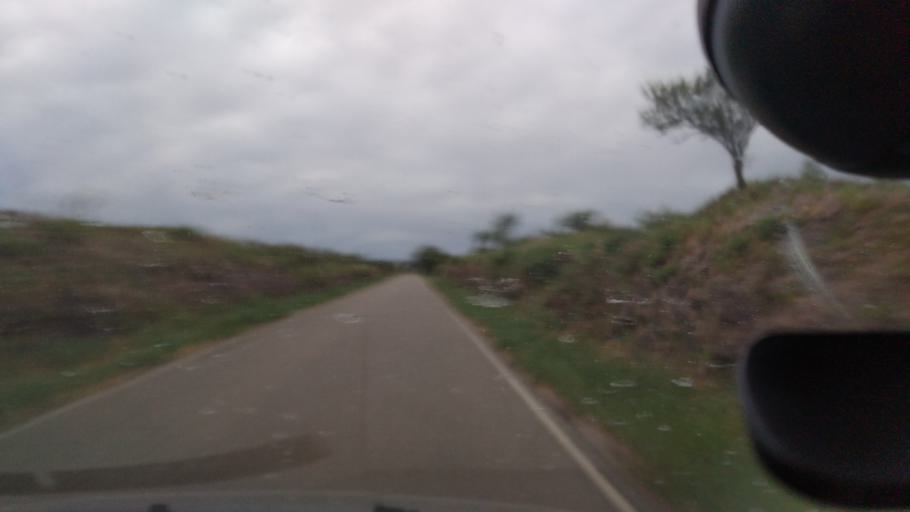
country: AR
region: Cordoba
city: Villa Las Rosas
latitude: -31.8919
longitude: -65.0318
